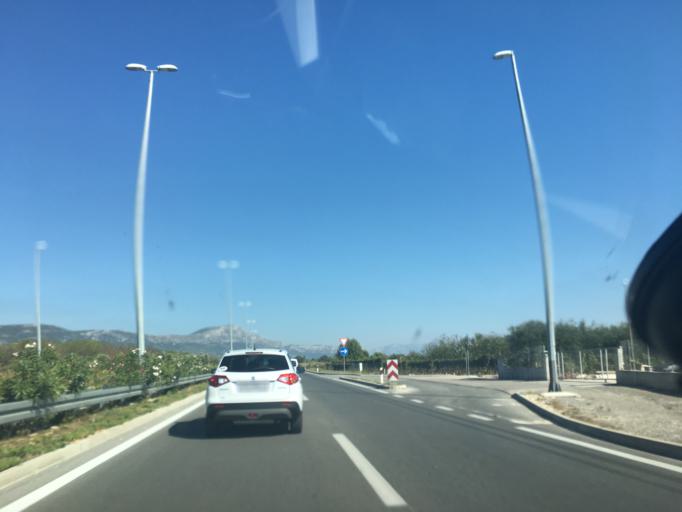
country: HR
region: Splitsko-Dalmatinska
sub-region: Grad Trogir
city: Trogir
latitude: 43.5500
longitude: 16.3075
